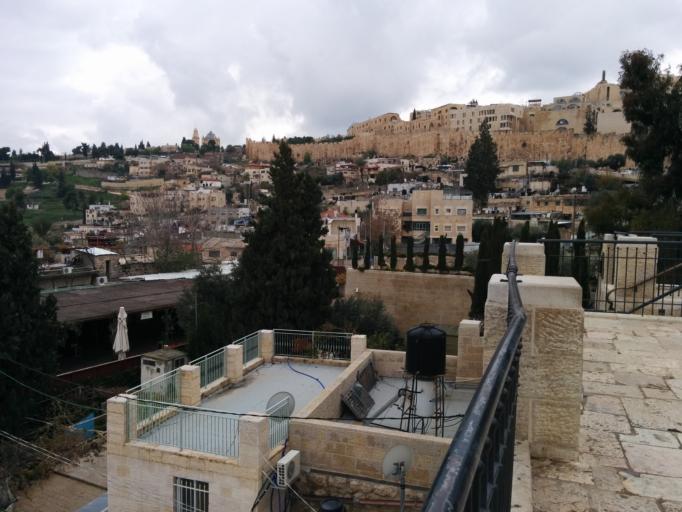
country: PS
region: West Bank
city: Old City
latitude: 31.7742
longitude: 35.2361
